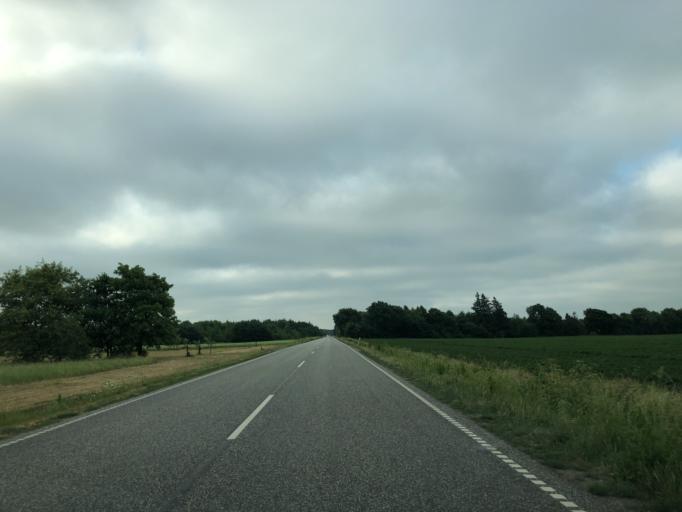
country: DK
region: South Denmark
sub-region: Vejle Kommune
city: Give
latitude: 55.8964
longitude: 9.2070
